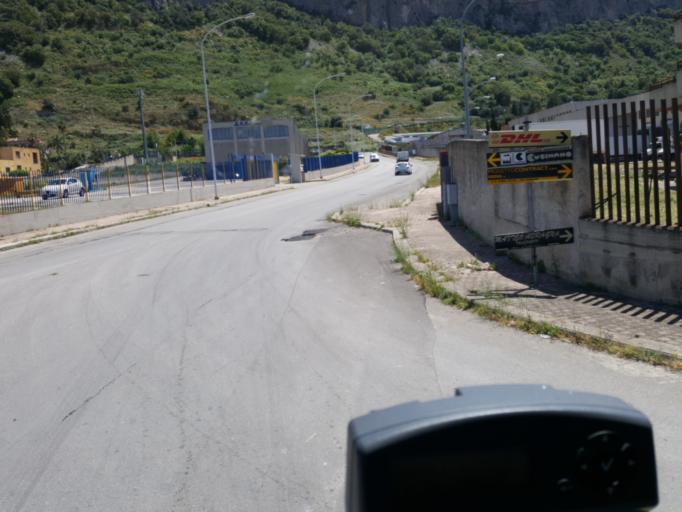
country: IT
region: Sicily
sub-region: Palermo
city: Carini
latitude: 38.1520
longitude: 13.2065
